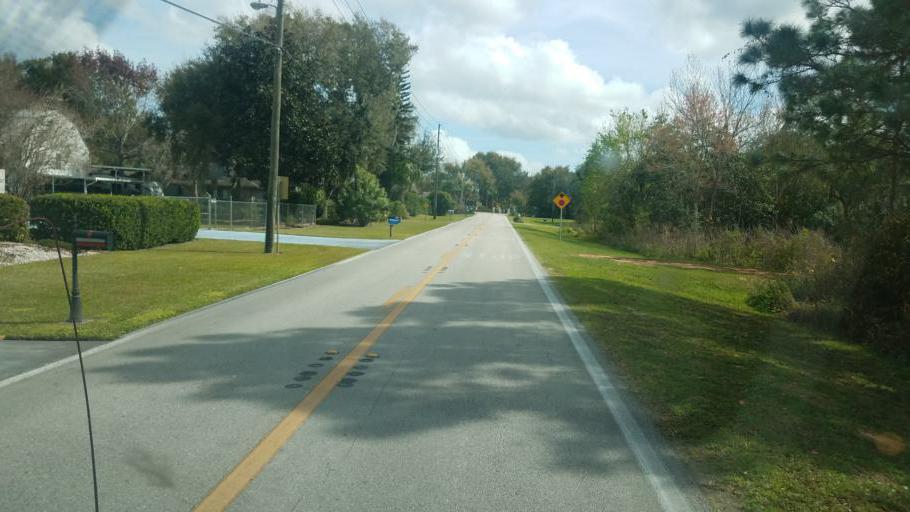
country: US
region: Florida
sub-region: Polk County
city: Dundee
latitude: 28.0556
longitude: -81.5350
